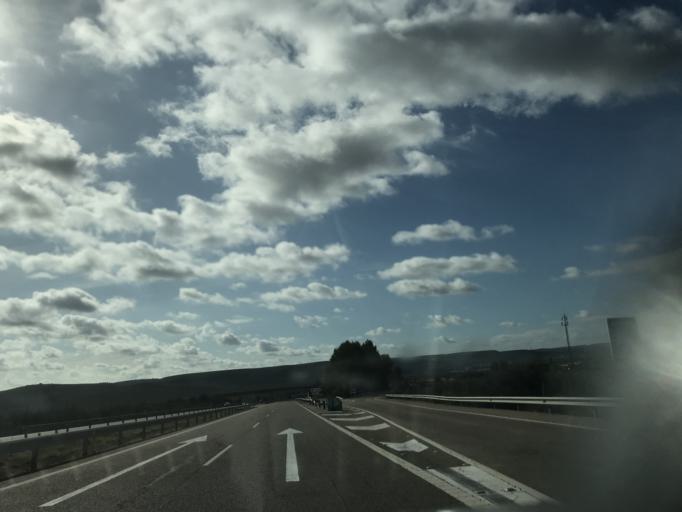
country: ES
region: Andalusia
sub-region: Province of Cordoba
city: Villa del Rio
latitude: 37.9938
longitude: -4.2533
